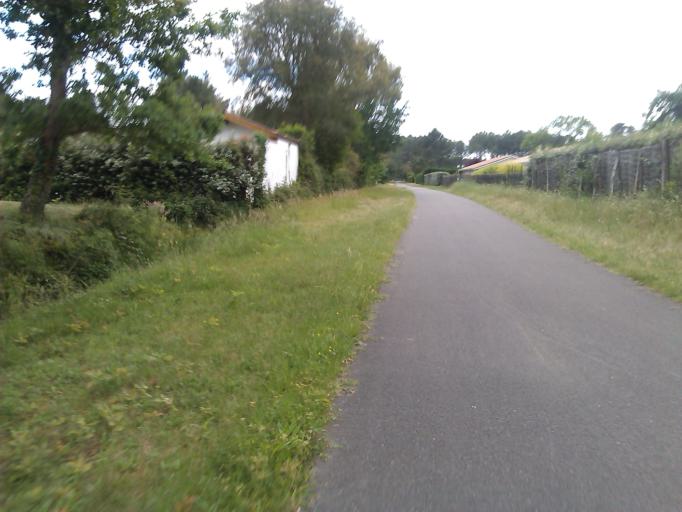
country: FR
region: Aquitaine
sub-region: Departement des Landes
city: Leon
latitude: 43.8469
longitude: -1.3534
